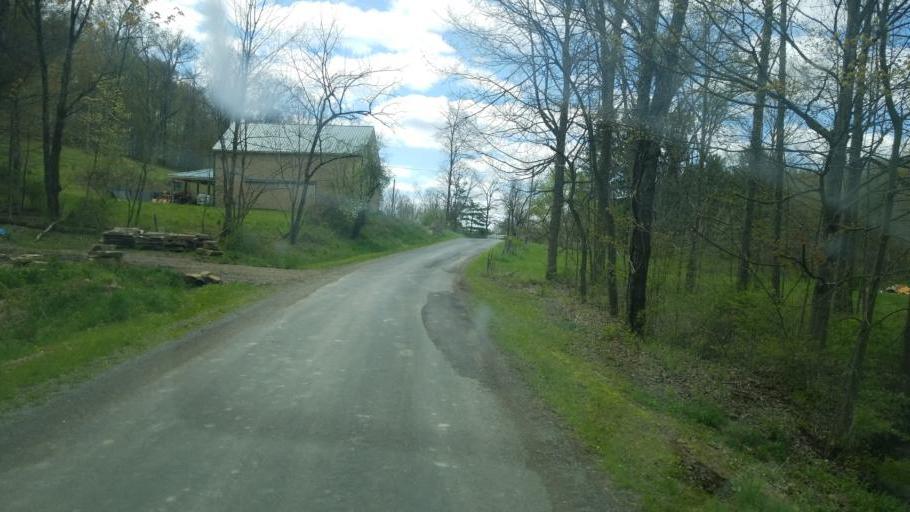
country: US
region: Ohio
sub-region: Knox County
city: Danville
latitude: 40.4829
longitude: -82.3360
